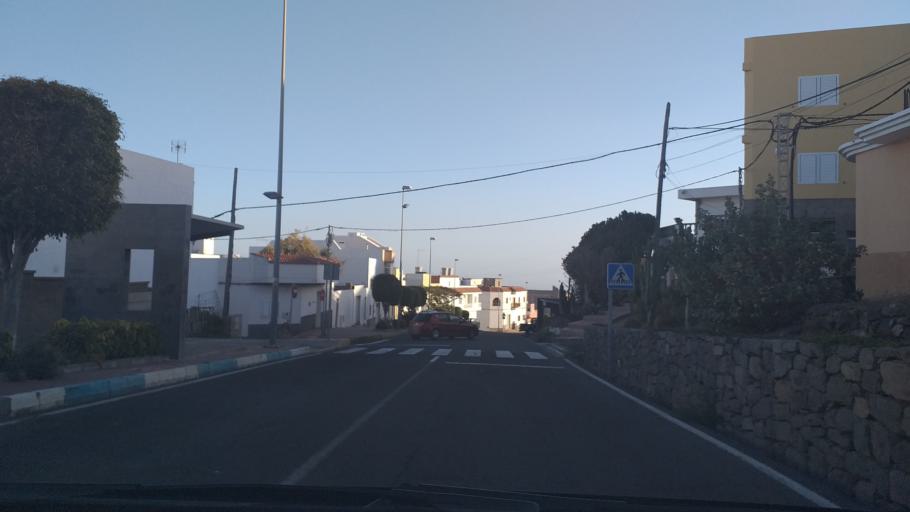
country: ES
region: Canary Islands
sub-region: Provincia de Las Palmas
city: Ingenio
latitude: 27.9212
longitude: -15.4488
